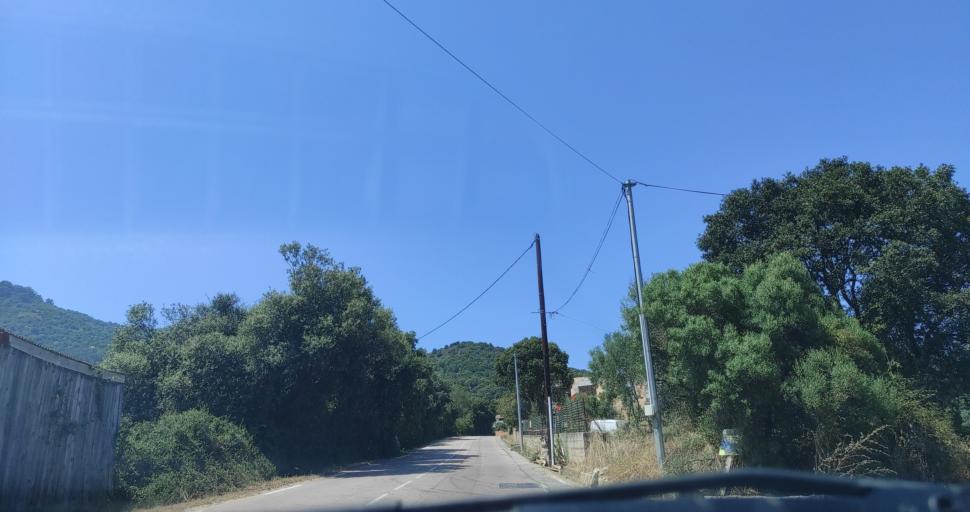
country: FR
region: Corsica
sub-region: Departement de la Corse-du-Sud
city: Alata
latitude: 41.9550
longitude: 8.7300
